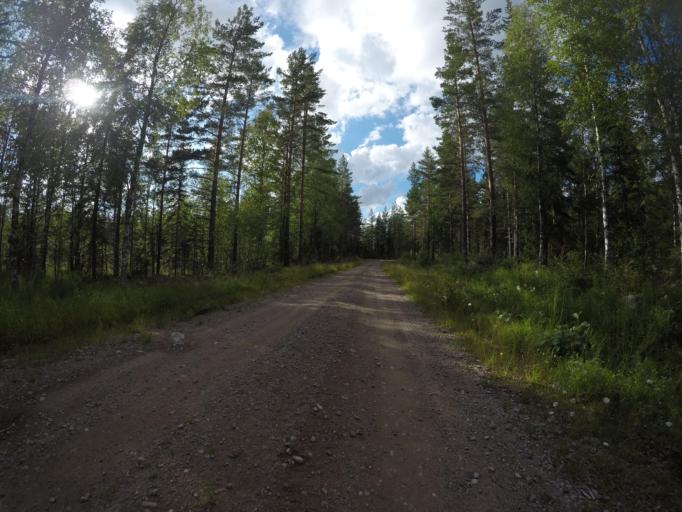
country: SE
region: OErebro
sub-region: Hallefors Kommun
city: Haellefors
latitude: 59.9597
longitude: 14.5626
